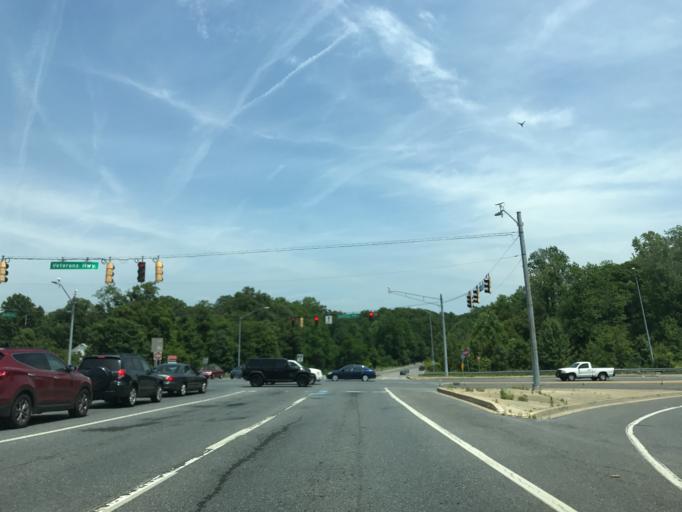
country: US
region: Maryland
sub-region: Anne Arundel County
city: South Gate
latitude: 39.0950
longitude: -76.6240
